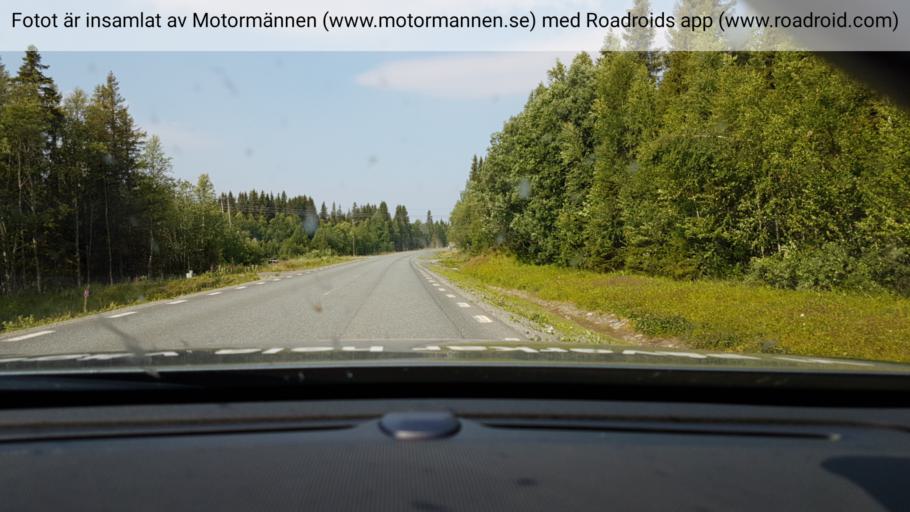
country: SE
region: Vaesterbotten
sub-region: Vilhelmina Kommun
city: Sjoberg
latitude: 65.4795
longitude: 15.8587
